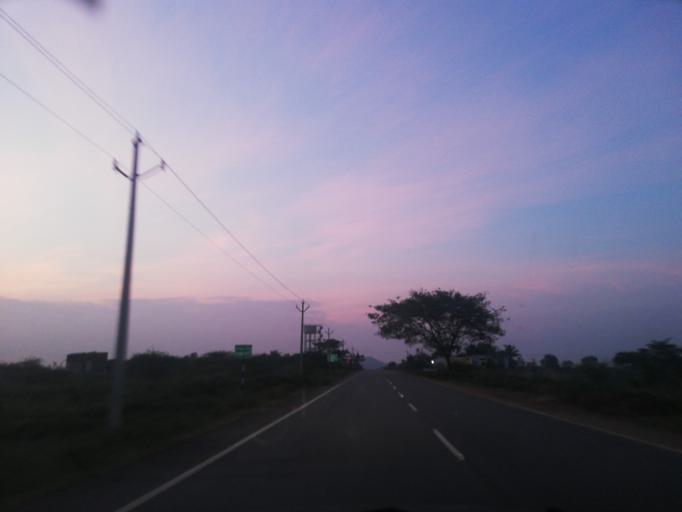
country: IN
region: Andhra Pradesh
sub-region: Guntur
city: Macherla
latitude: 16.6904
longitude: 79.2497
